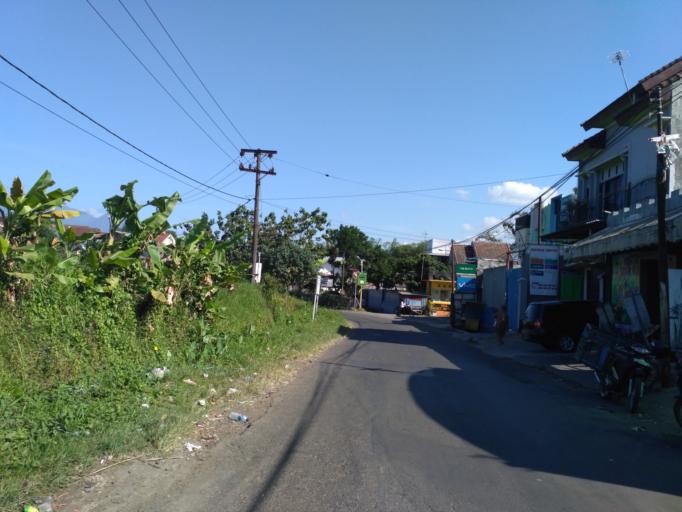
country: ID
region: East Java
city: Singosari
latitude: -7.9164
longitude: 112.6631
